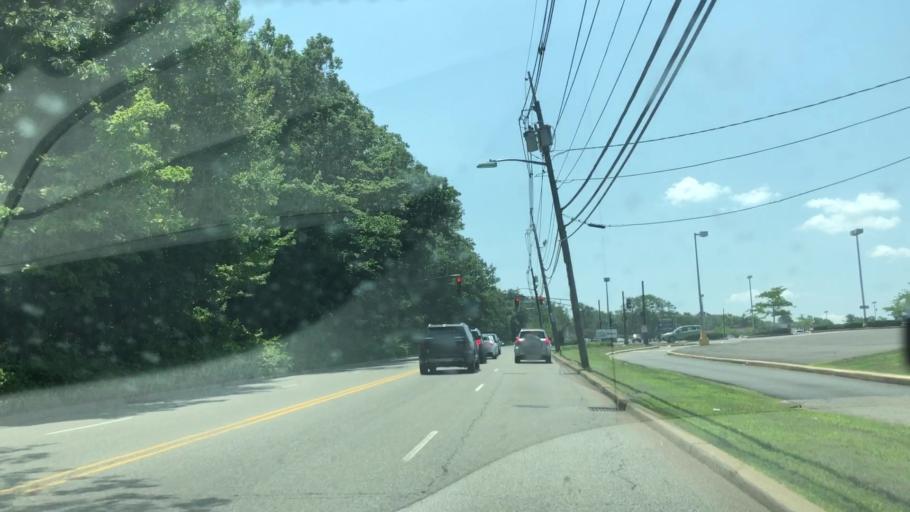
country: US
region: New Jersey
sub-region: Essex County
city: West Orange
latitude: 40.8067
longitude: -74.2466
